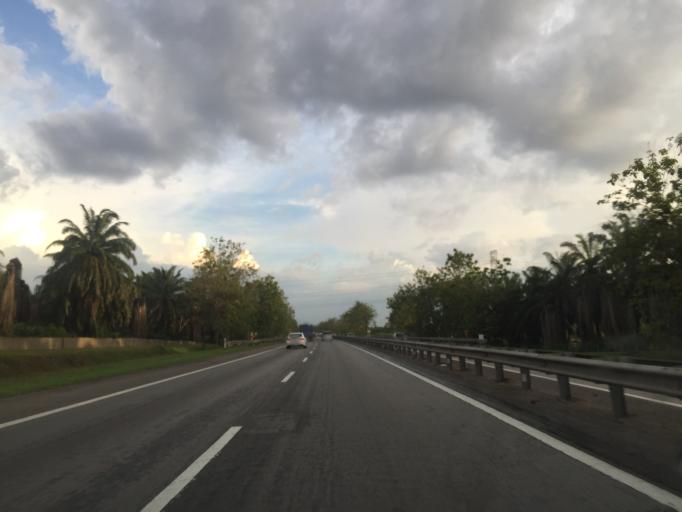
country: MY
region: Kedah
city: Bedong
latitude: 5.7551
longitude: 100.5081
